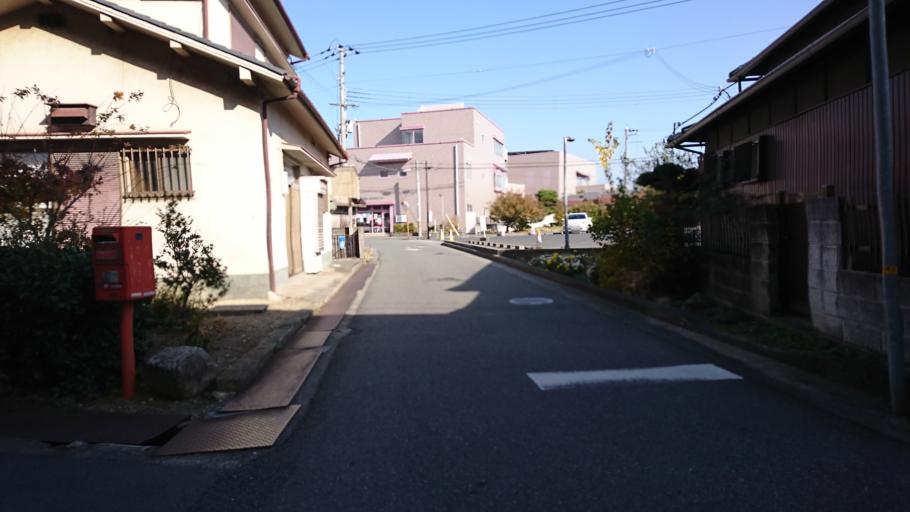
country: JP
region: Hyogo
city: Kakogawacho-honmachi
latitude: 34.7193
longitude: 134.8677
